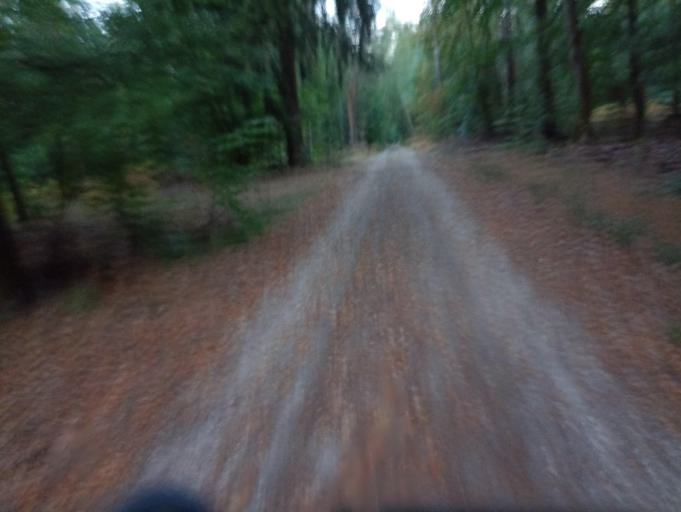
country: DE
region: Hesse
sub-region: Regierungsbezirk Darmstadt
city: Erzhausen
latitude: 49.9716
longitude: 8.6180
